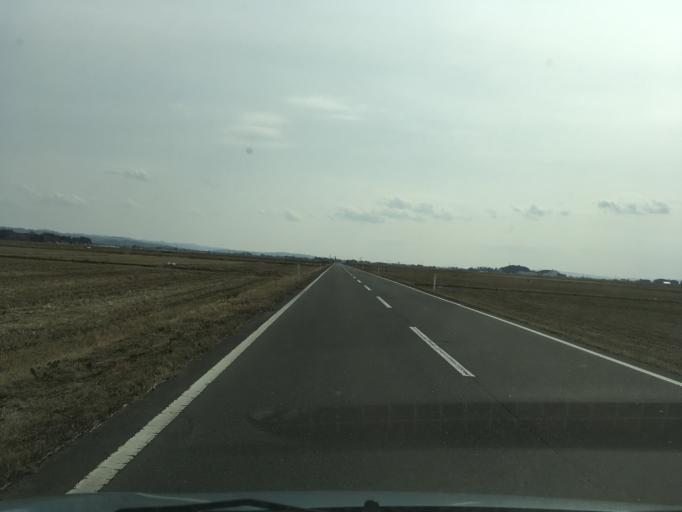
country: JP
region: Iwate
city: Ichinoseki
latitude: 38.7540
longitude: 141.2364
